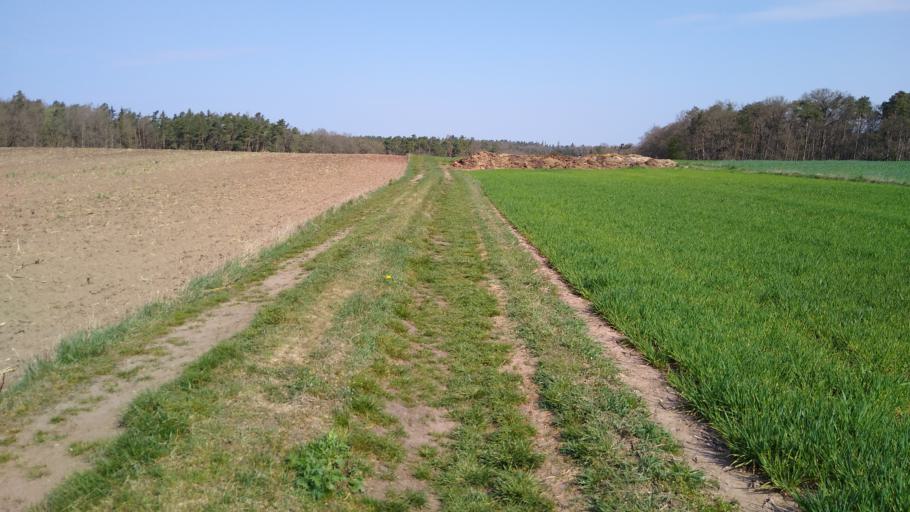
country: DE
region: Bavaria
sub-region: Regierungsbezirk Mittelfranken
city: Obermichelbach
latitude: 49.5014
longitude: 10.9223
